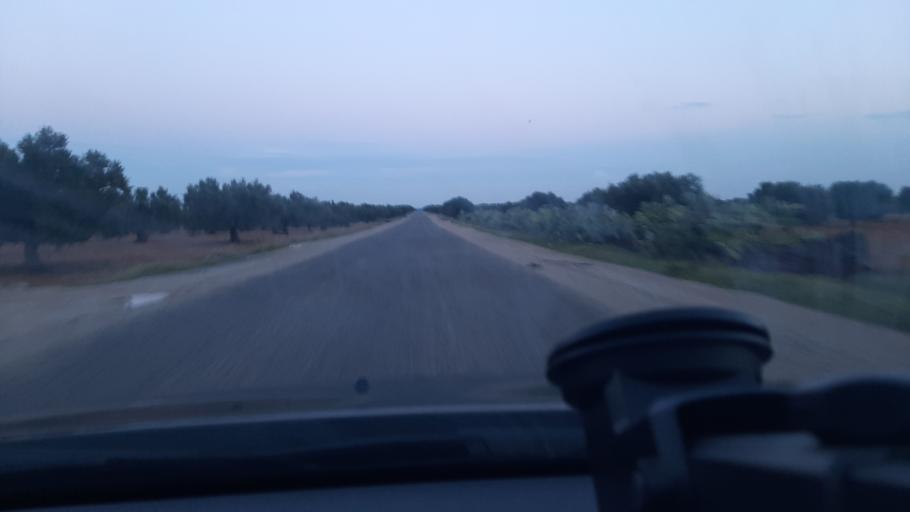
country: TN
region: Al Mahdiyah
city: Shurban
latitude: 35.0306
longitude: 10.4906
